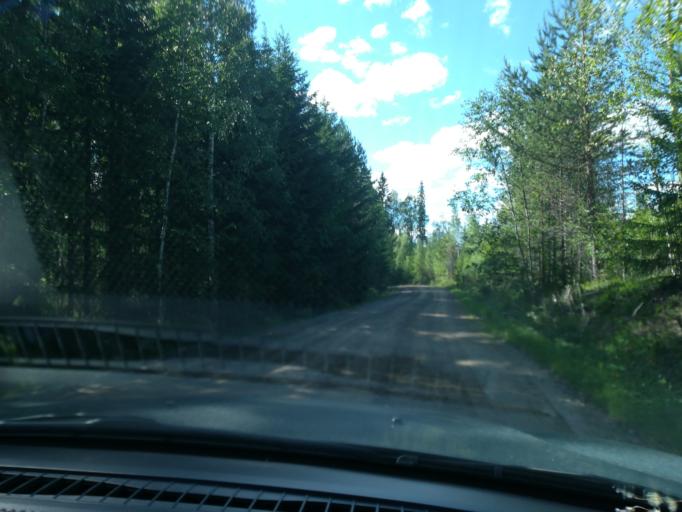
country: FI
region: Southern Savonia
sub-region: Mikkeli
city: Puumala
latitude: 61.6542
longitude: 28.1698
